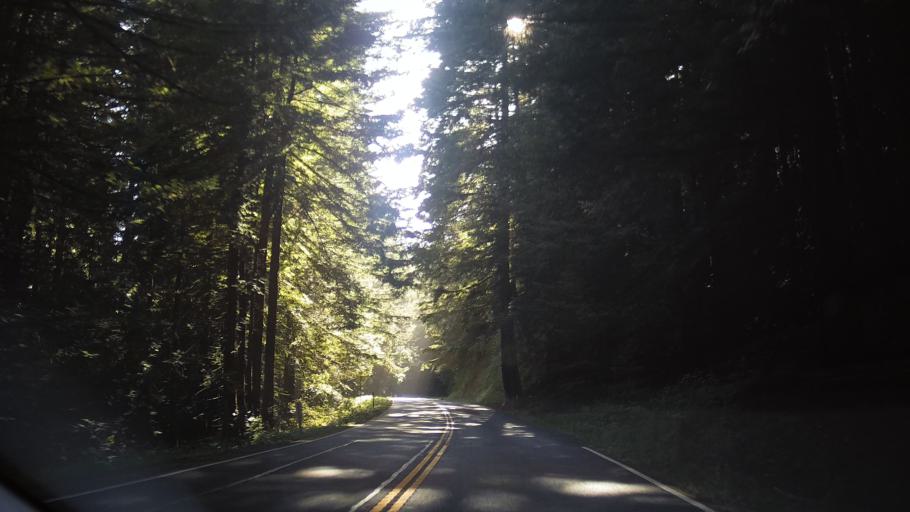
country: US
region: California
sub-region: Mendocino County
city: Brooktrails
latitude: 39.3489
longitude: -123.5847
